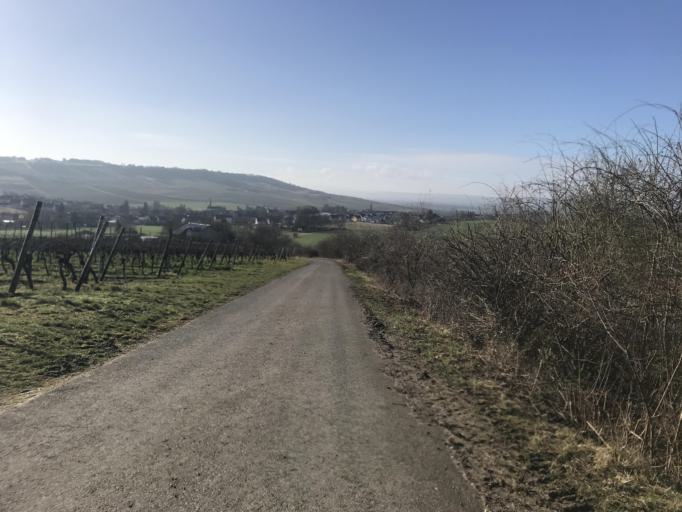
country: DE
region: Rheinland-Pfalz
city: Sankt Johann
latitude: 49.8756
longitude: 8.0183
